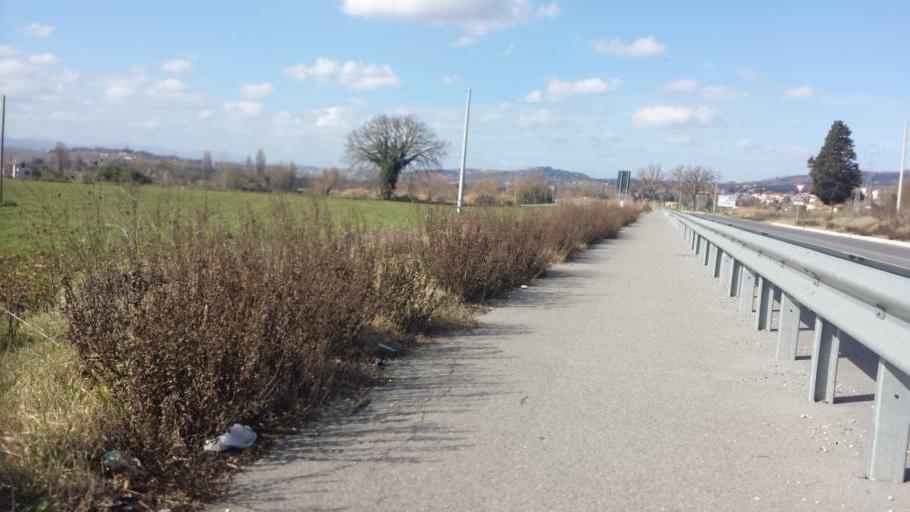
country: IT
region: Umbria
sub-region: Provincia di Terni
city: Terni
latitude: 42.5763
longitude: 12.5974
